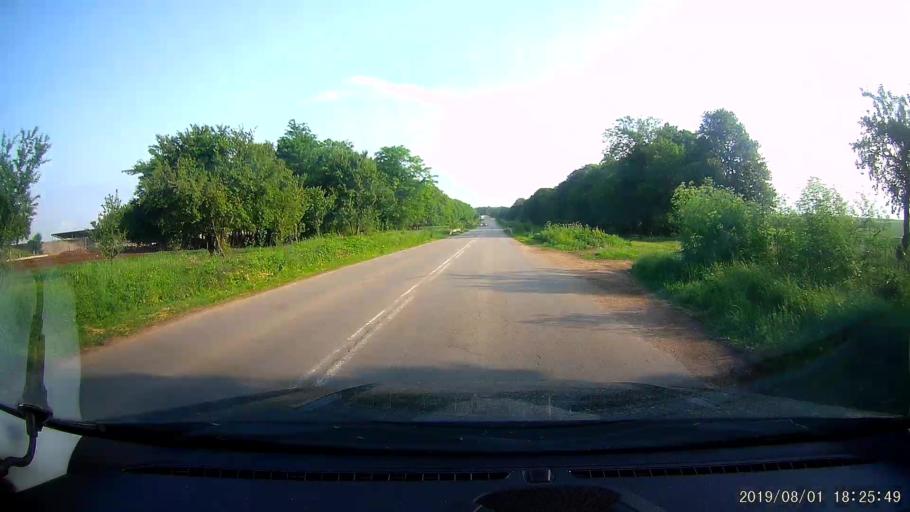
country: BG
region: Shumen
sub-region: Obshtina Venets
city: Venets
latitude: 43.6121
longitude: 26.9953
